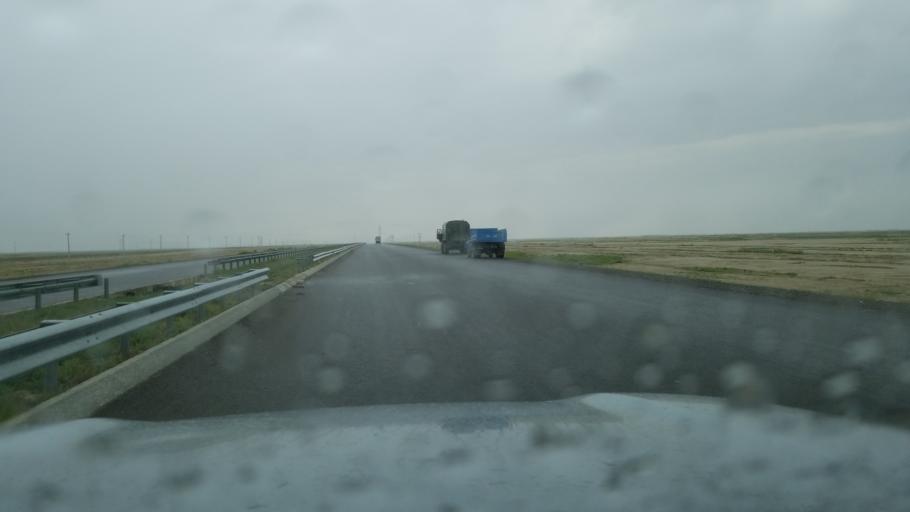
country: TM
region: Balkan
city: Serdar
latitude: 39.0161
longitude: 56.2216
